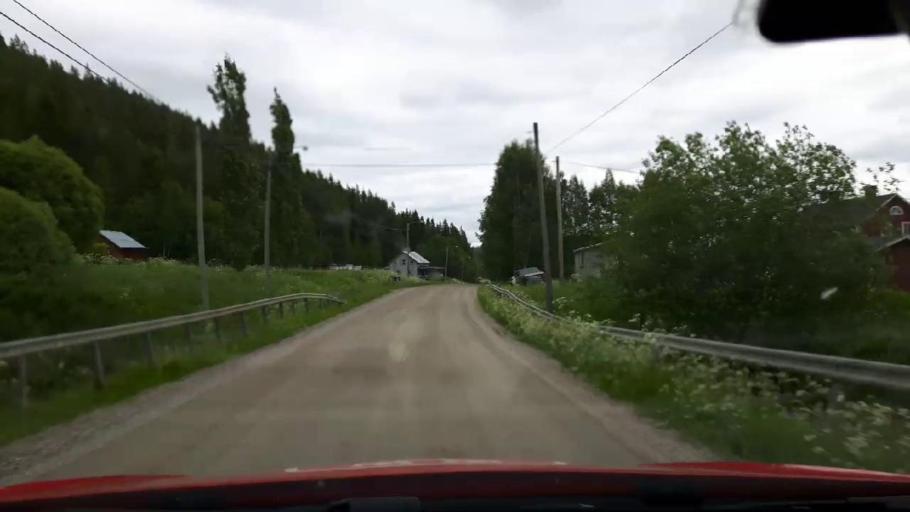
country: SE
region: Jaemtland
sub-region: Ragunda Kommun
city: Hammarstrand
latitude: 63.1720
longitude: 16.2038
